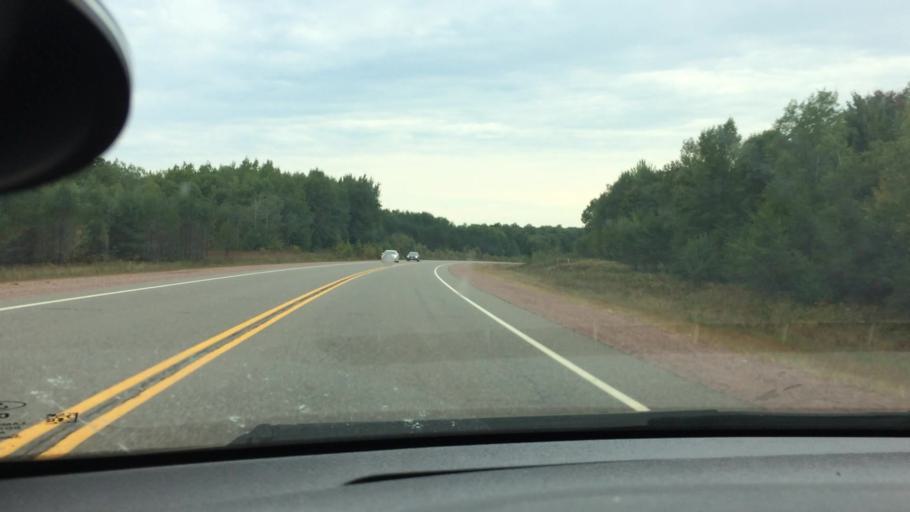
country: US
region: Wisconsin
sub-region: Clark County
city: Neillsville
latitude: 44.5677
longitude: -90.7226
